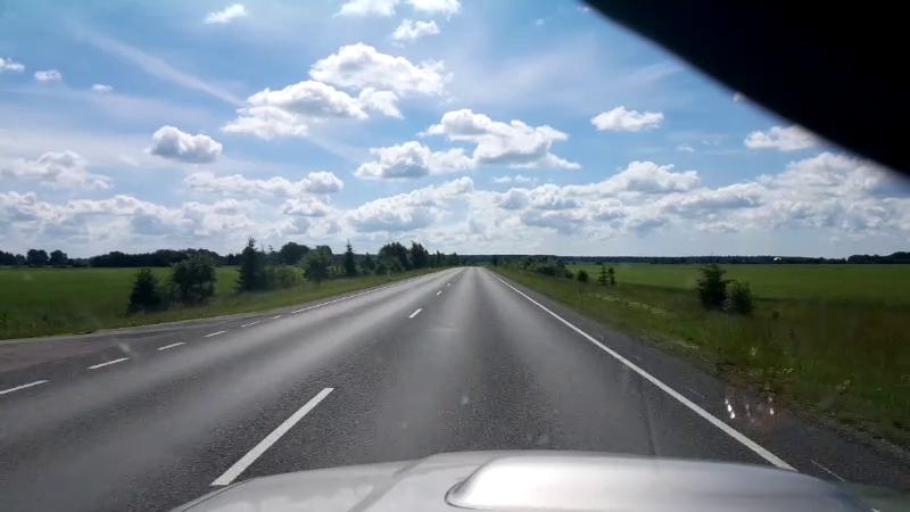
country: EE
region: Jaervamaa
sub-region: Jaerva-Jaani vald
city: Jarva-Jaani
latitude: 59.1562
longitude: 25.7660
